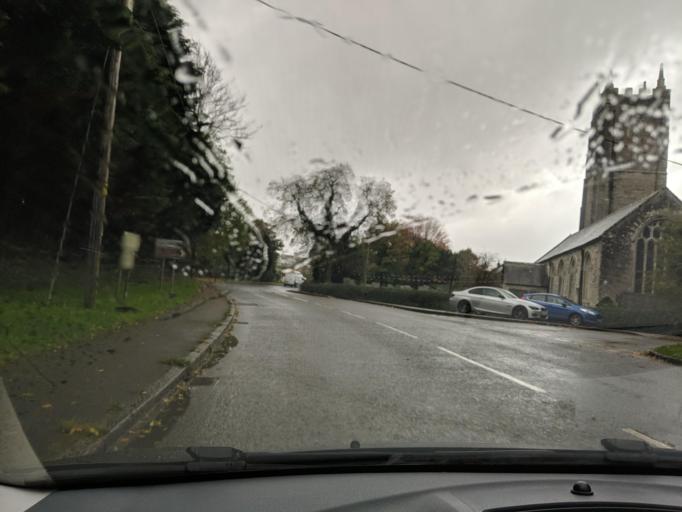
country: GB
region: England
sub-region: Cornwall
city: Wadebridge
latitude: 50.5125
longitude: -4.8204
